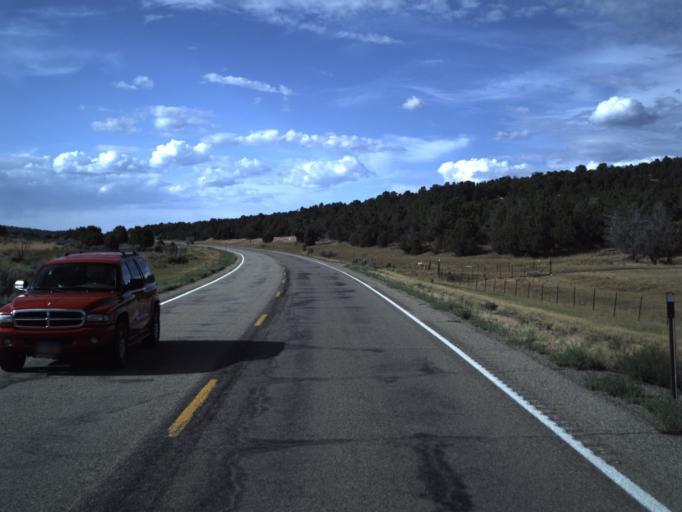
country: US
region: Utah
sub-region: Sanpete County
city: Fairview
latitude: 39.6564
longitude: -111.4503
